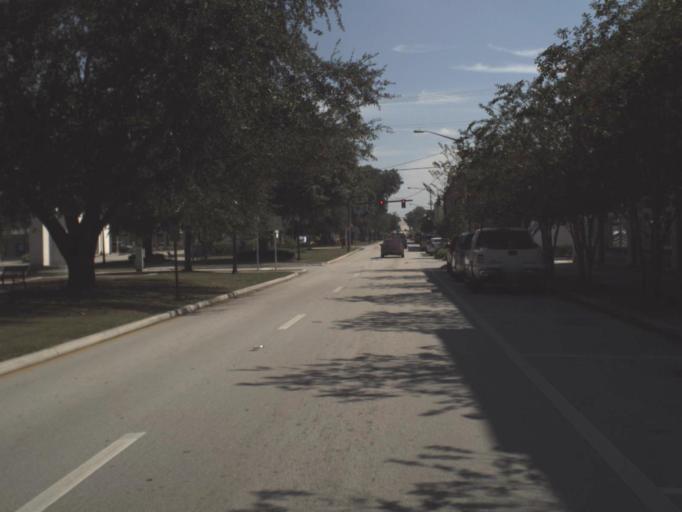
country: US
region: Florida
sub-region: Highlands County
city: Avon Park
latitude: 27.5956
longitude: -81.5036
